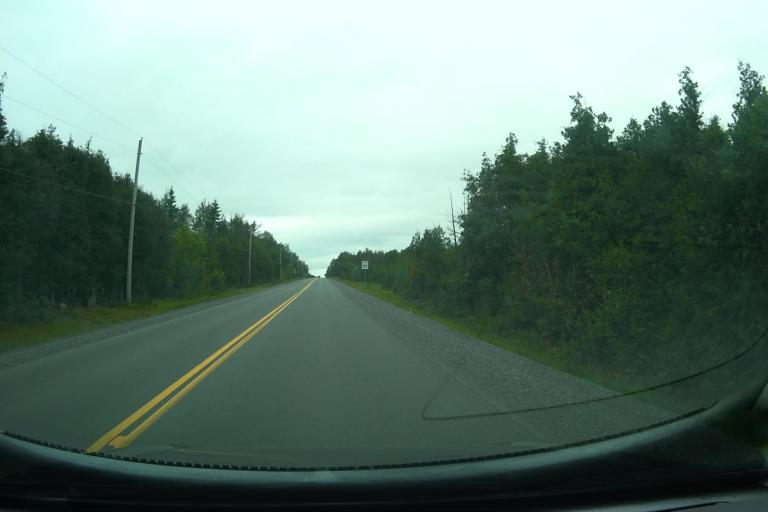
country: CA
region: Ontario
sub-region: Lanark County
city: Smiths Falls
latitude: 44.9626
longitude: -75.7708
